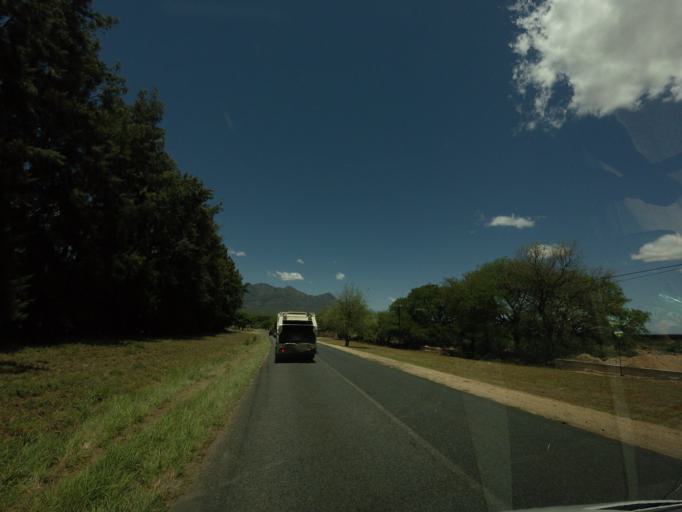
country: ZA
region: Limpopo
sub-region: Mopani District Municipality
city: Hoedspruit
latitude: -24.3996
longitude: 30.8058
